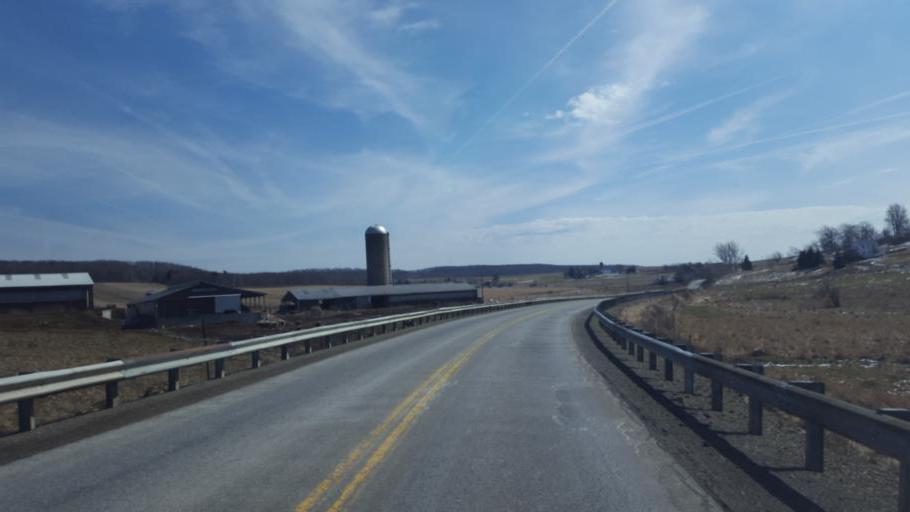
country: US
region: Pennsylvania
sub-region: Potter County
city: Galeton
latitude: 41.8945
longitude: -77.7477
